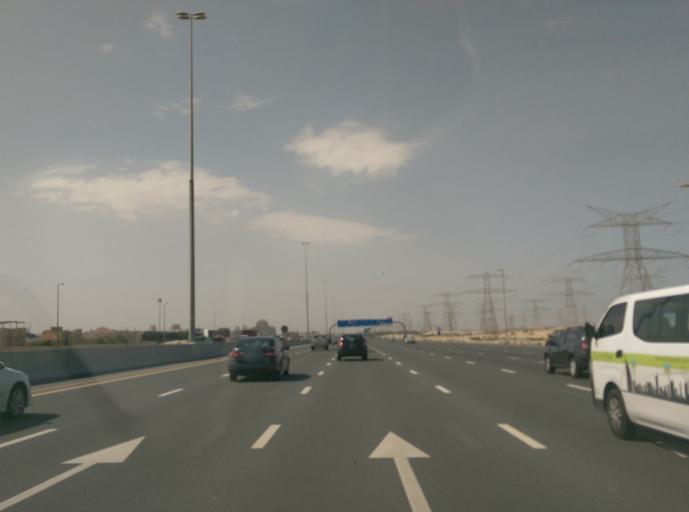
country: AE
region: Dubai
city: Dubai
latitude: 25.0875
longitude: 55.2197
